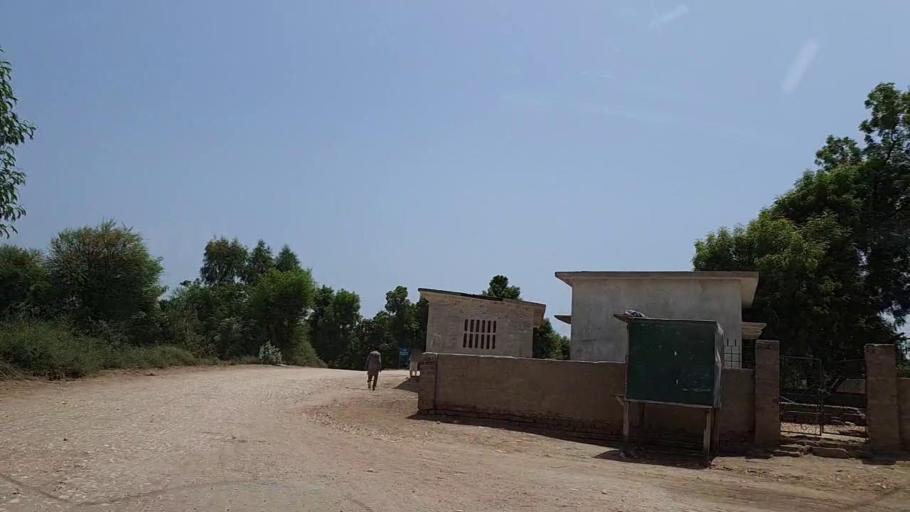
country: PK
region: Sindh
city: Tharu Shah
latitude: 26.9683
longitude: 68.0415
